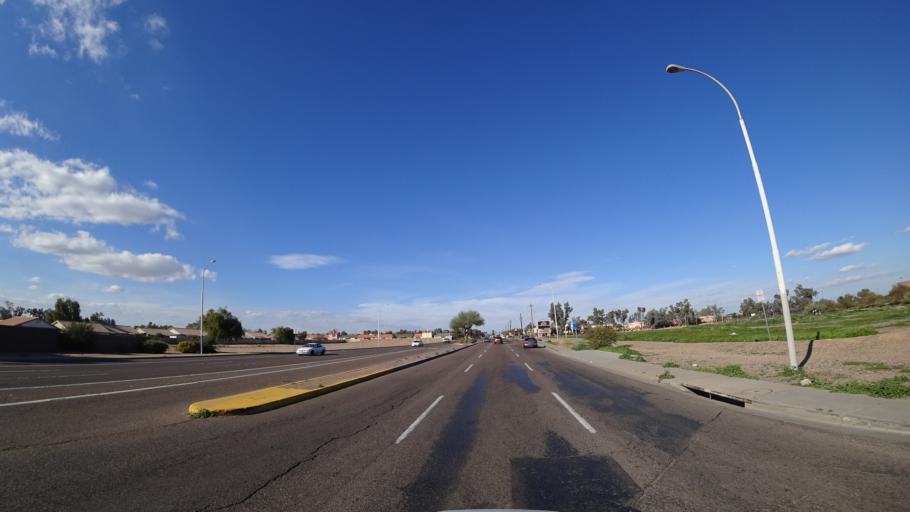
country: US
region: Arizona
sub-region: Maricopa County
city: Tolleson
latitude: 33.4689
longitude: -112.2378
